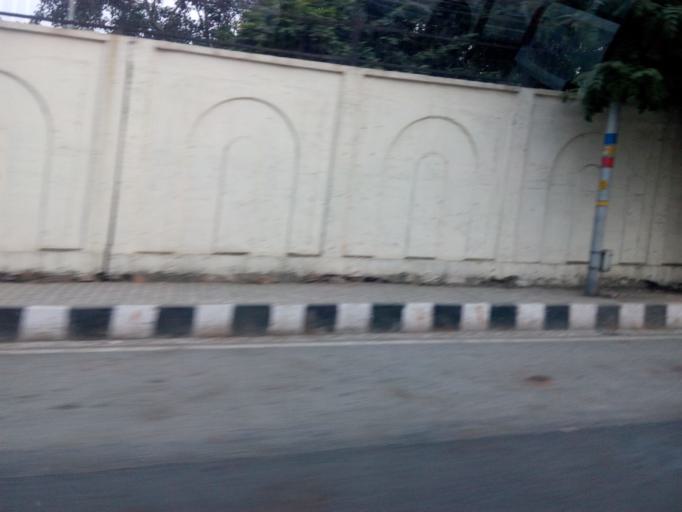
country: IN
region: NCT
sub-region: Central Delhi
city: Karol Bagh
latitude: 28.5648
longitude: 77.1250
